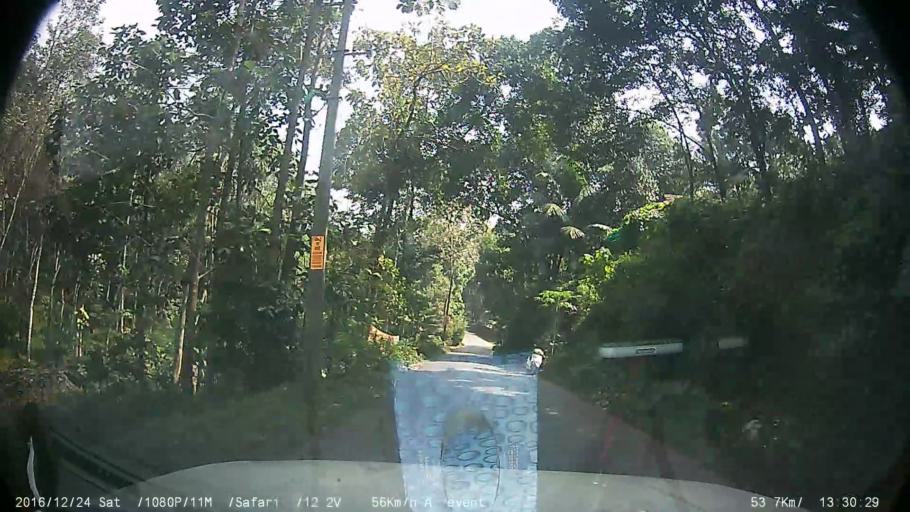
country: IN
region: Kerala
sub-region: Kottayam
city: Palackattumala
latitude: 9.8475
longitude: 76.7021
